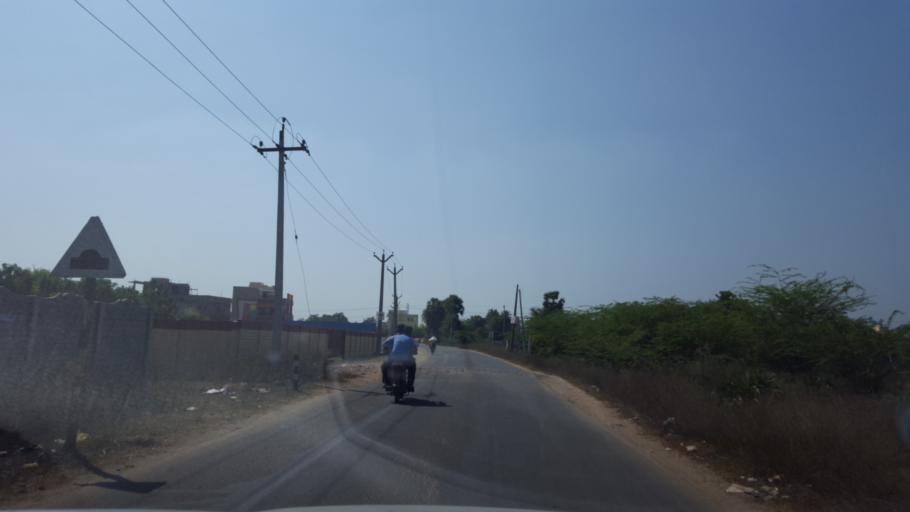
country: IN
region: Tamil Nadu
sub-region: Kancheepuram
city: Kanchipuram
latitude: 12.8387
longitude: 79.7258
